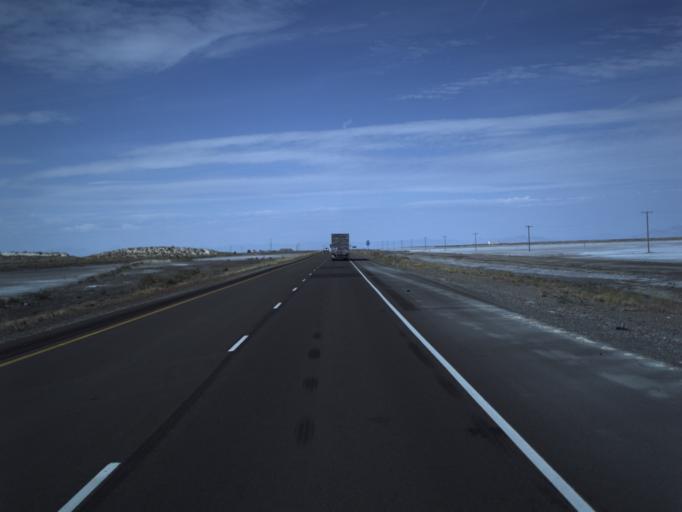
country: US
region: Utah
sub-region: Tooele County
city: Wendover
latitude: 40.7275
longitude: -113.2683
